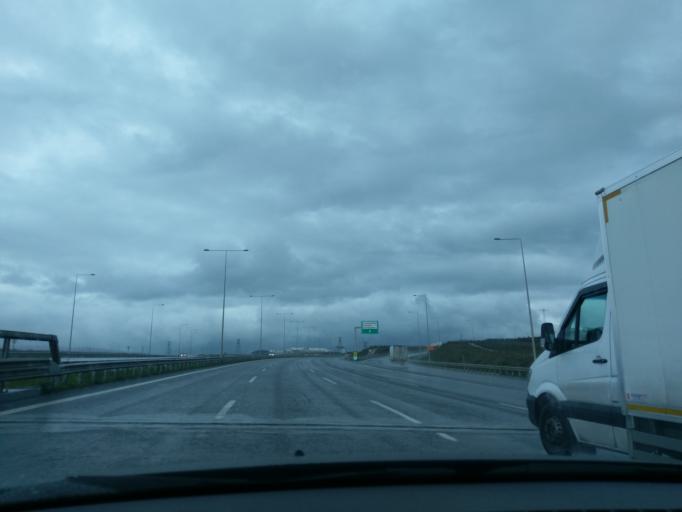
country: TR
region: Istanbul
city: Basaksehir
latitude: 41.1332
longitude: 28.8045
